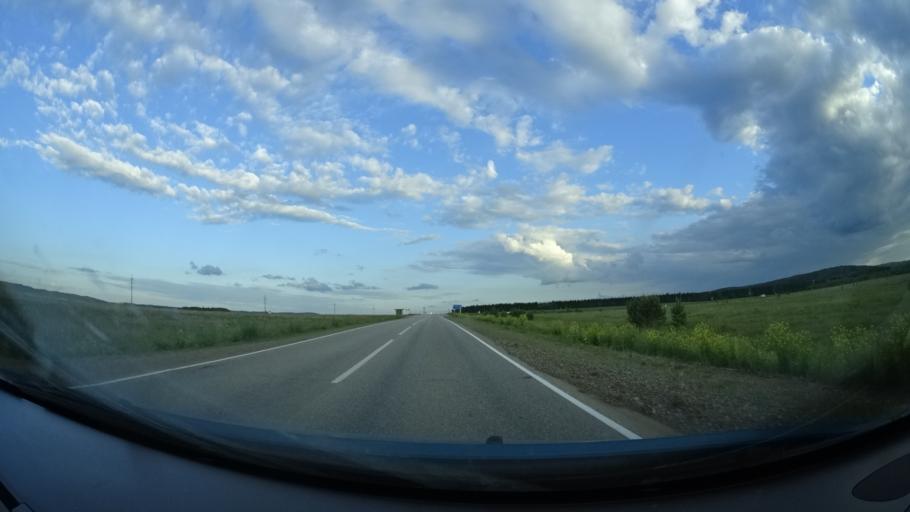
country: RU
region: Perm
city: Barda
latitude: 57.0241
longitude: 55.5541
